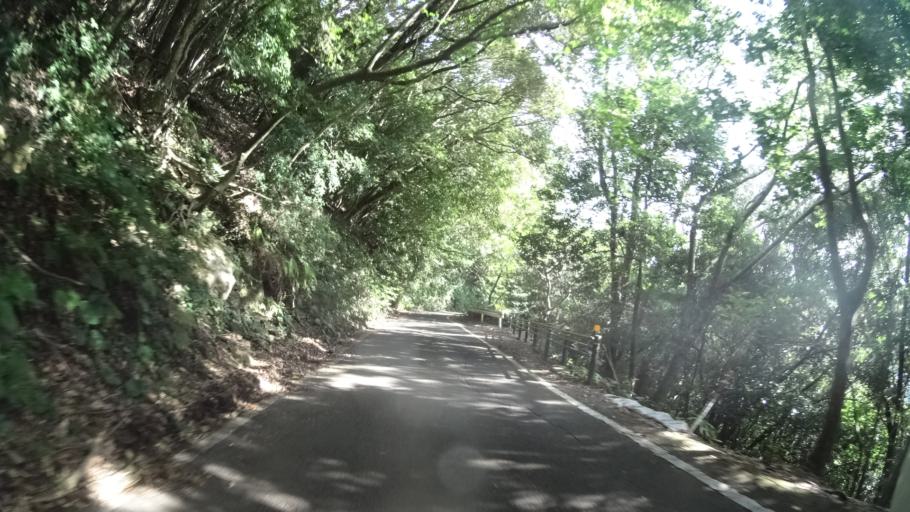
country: JP
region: Kagoshima
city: Nishinoomote
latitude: 30.3386
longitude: 130.3961
